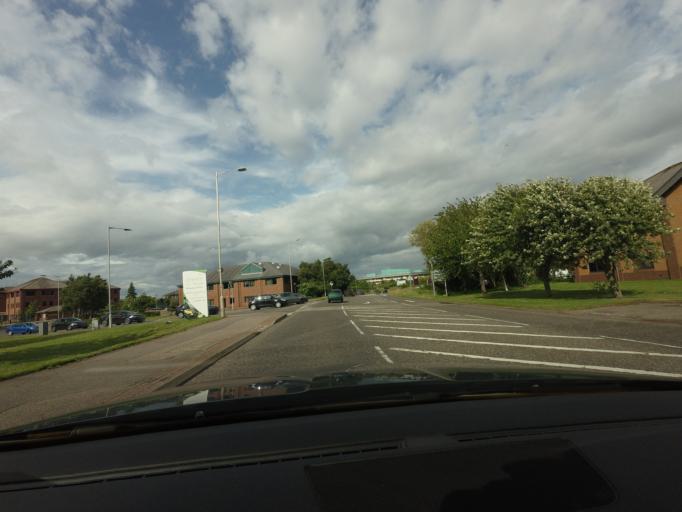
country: GB
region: Scotland
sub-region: Highland
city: Inverness
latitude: 57.4734
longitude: -4.1889
